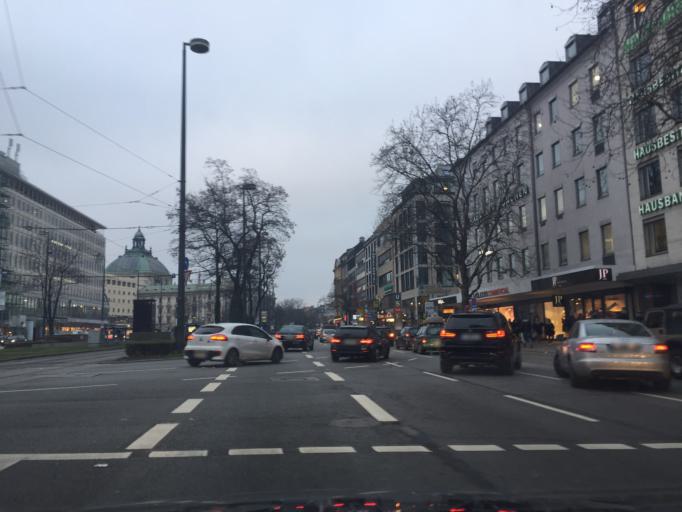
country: DE
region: Bavaria
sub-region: Upper Bavaria
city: Munich
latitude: 48.1373
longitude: 11.5653
